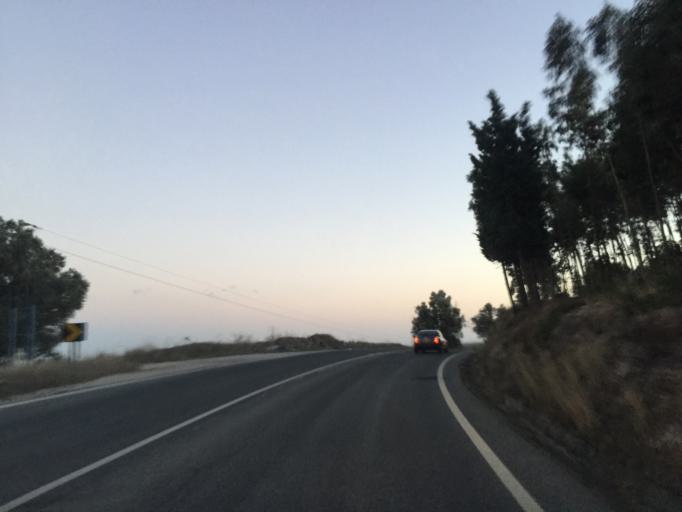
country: PT
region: Lisbon
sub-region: Alenquer
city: Alenquer
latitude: 39.1275
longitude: -8.9915
